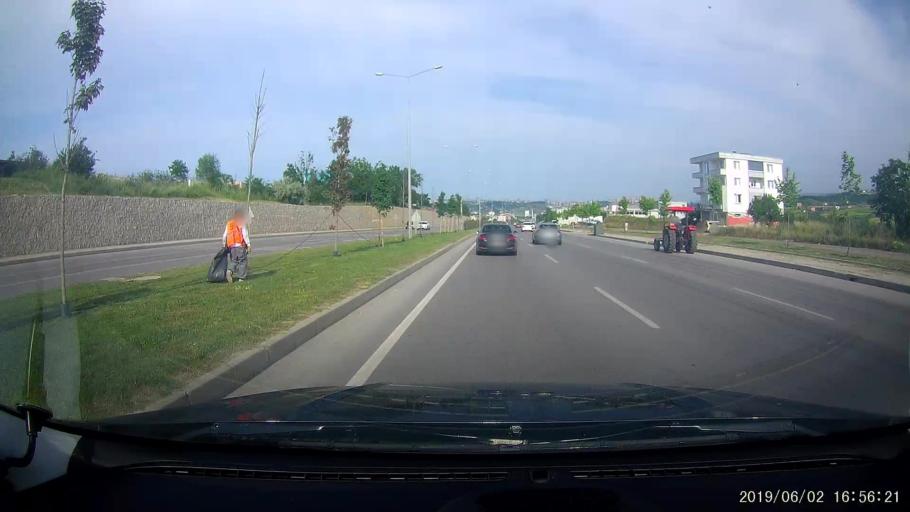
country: TR
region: Samsun
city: Samsun
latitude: 41.2928
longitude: 36.2585
